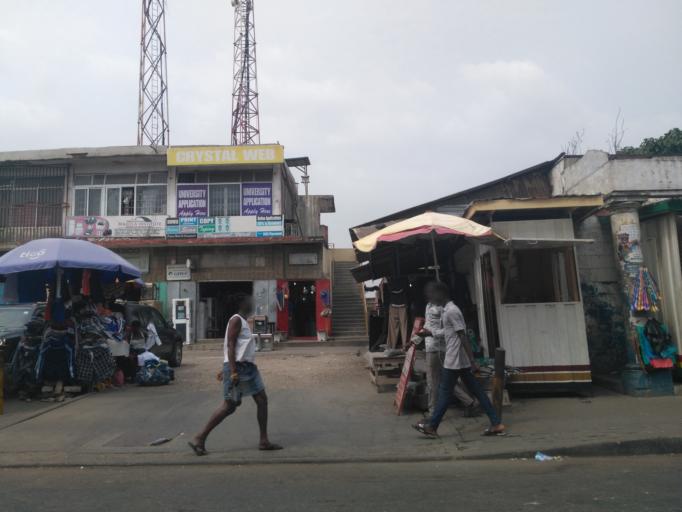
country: GH
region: Greater Accra
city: Accra
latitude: 5.5422
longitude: -0.2085
